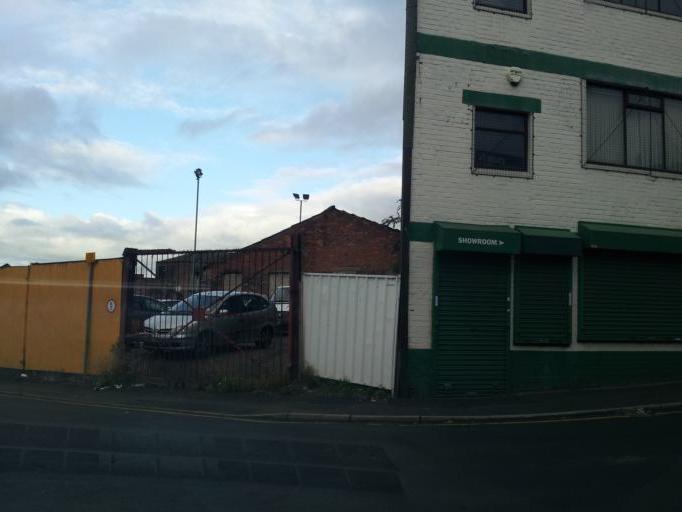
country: GB
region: England
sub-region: Manchester
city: Cheetham Hill
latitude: 53.4896
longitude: -2.2425
